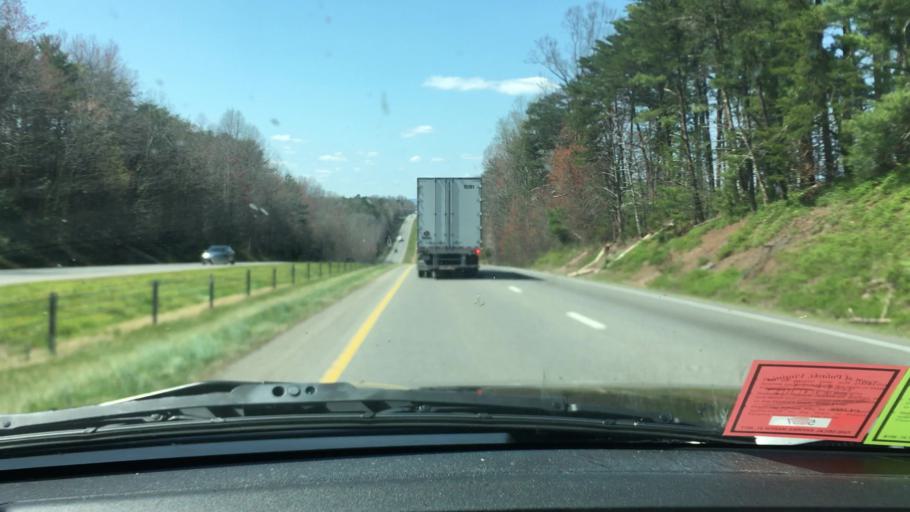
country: US
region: North Carolina
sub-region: Surry County
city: Pilot Mountain
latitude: 36.4222
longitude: -80.5160
